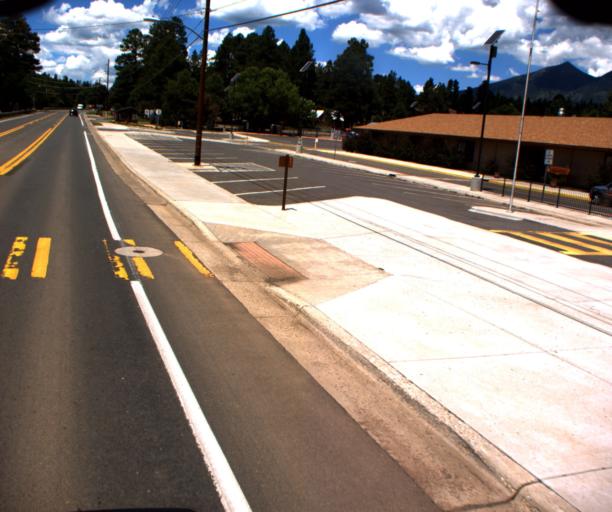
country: US
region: Arizona
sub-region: Coconino County
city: Flagstaff
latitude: 35.2222
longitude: -111.6537
